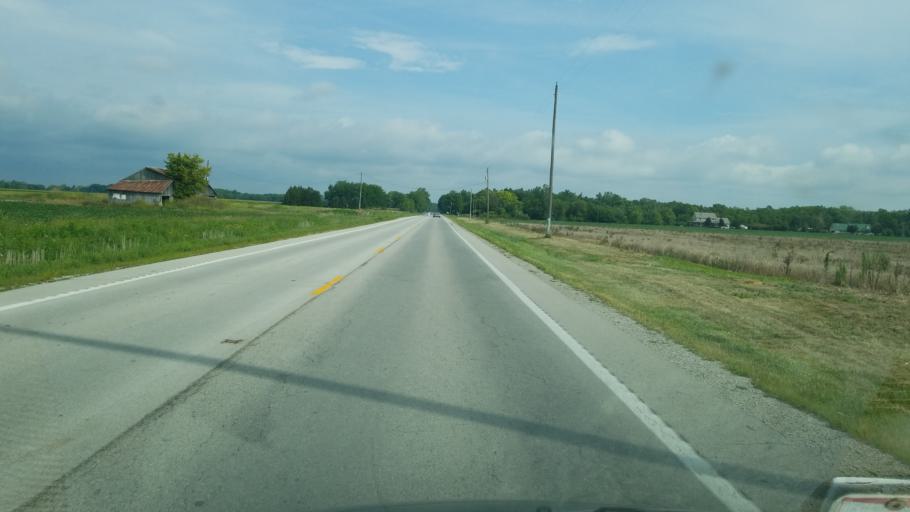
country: US
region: Ohio
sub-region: Sandusky County
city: Ballville
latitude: 41.2588
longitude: -83.1677
